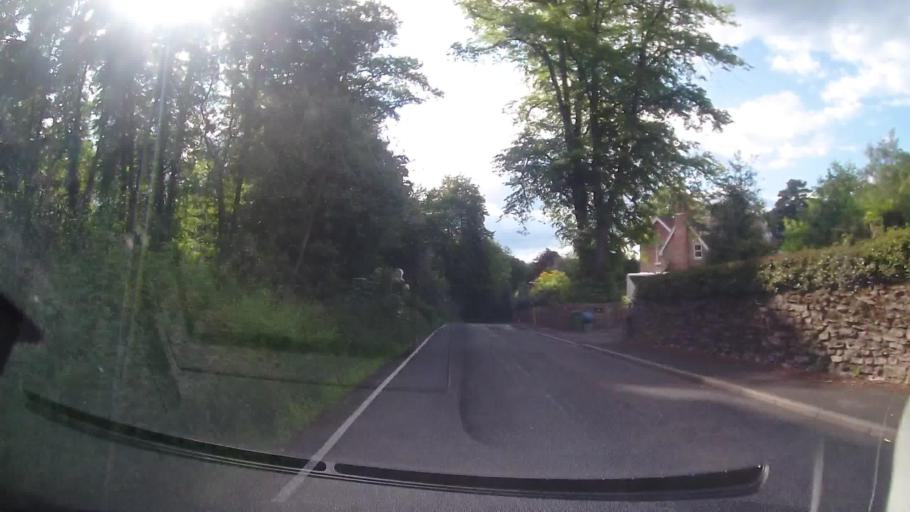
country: GB
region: England
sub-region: Shropshire
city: Much Wenlock
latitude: 52.6443
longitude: -2.5741
